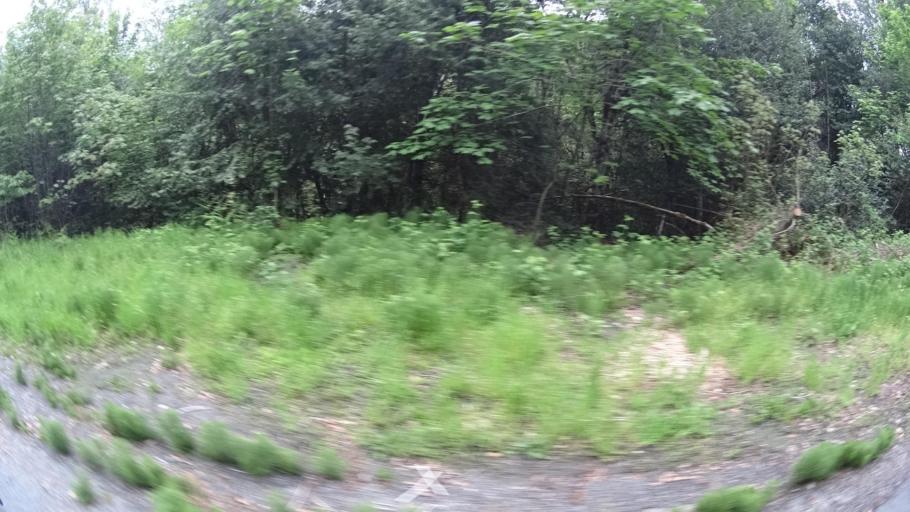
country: US
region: California
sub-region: Humboldt County
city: Blue Lake
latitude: 40.9534
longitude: -123.8383
